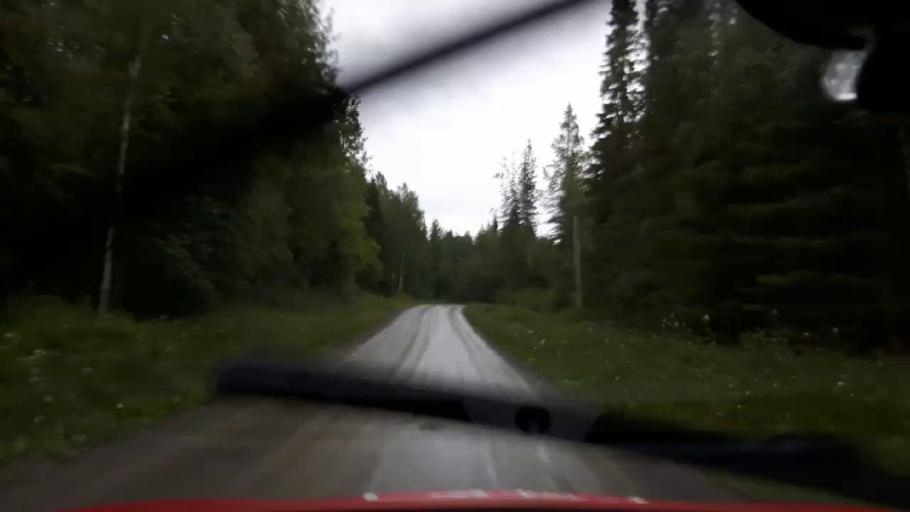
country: SE
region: Jaemtland
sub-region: OEstersunds Kommun
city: Brunflo
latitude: 62.8999
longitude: 14.8623
